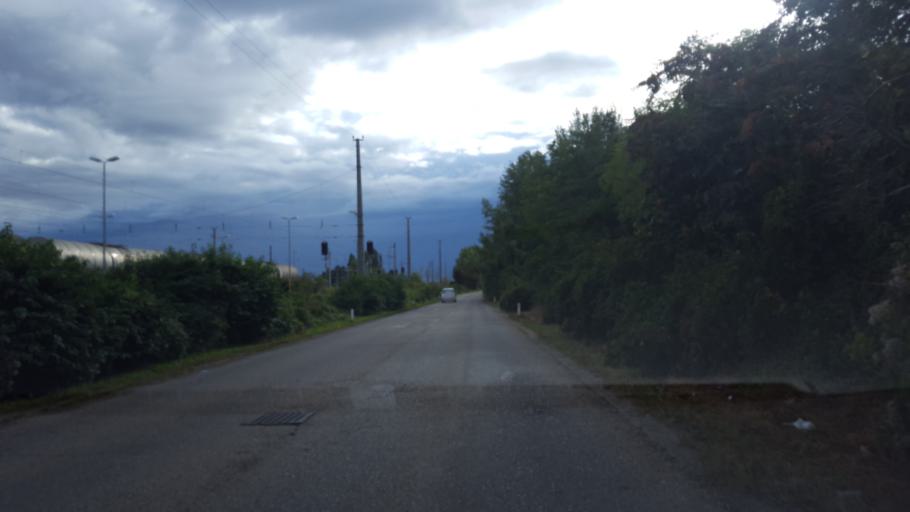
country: AT
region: Lower Austria
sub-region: Politischer Bezirk Wien-Umgebung
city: Schwechat
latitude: 48.1440
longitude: 16.4612
